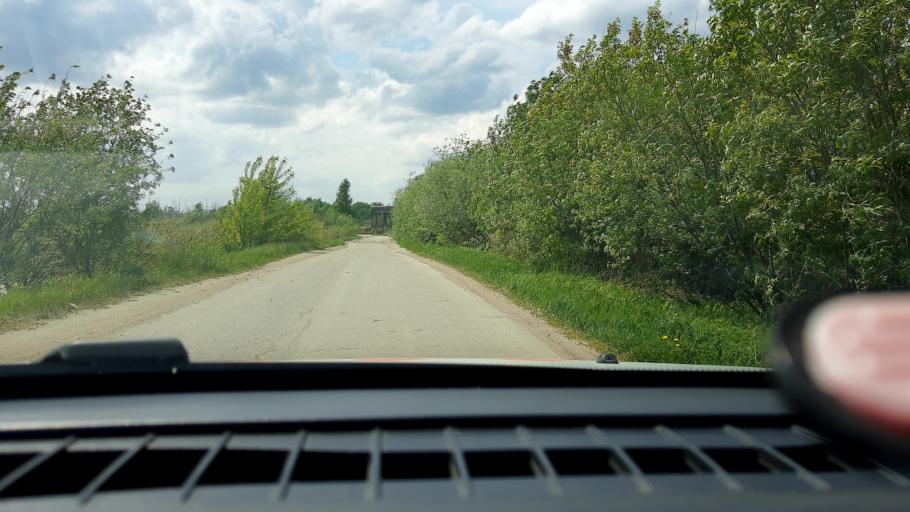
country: RU
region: Nizjnij Novgorod
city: Kstovo
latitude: 56.1354
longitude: 44.1284
